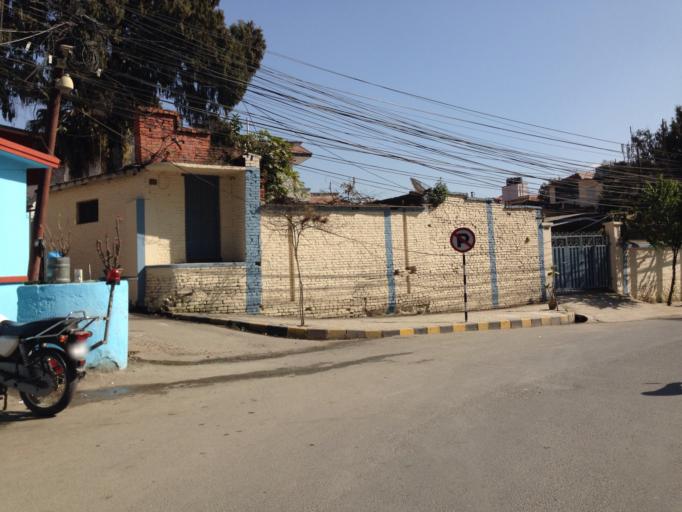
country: NP
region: Central Region
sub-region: Bagmati Zone
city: Kathmandu
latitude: 27.7264
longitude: 85.3306
